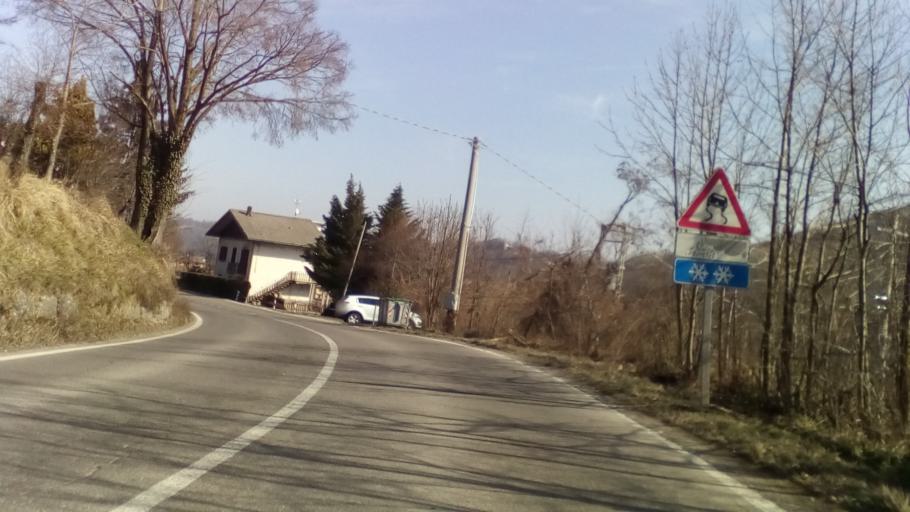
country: IT
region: Emilia-Romagna
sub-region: Provincia di Modena
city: Pavullo nel Frignano
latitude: 44.3089
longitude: 10.8212
